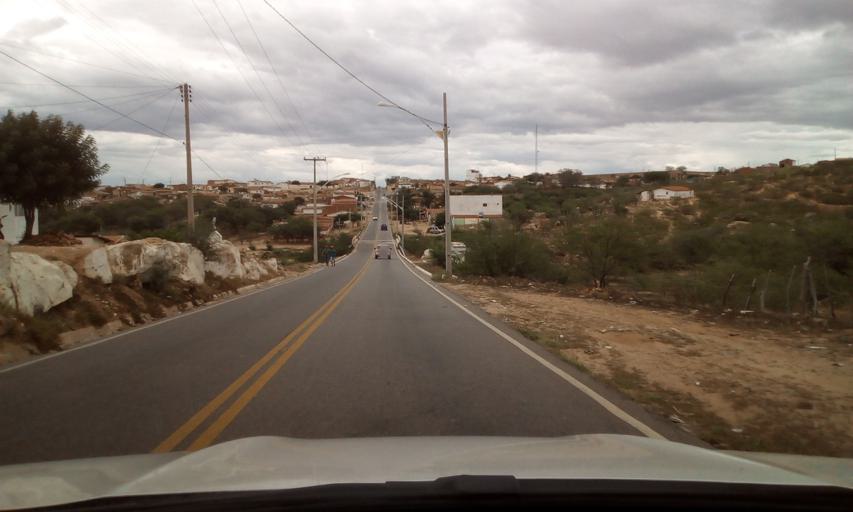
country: BR
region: Paraiba
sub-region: Picui
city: Picui
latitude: -6.5141
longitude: -36.3358
